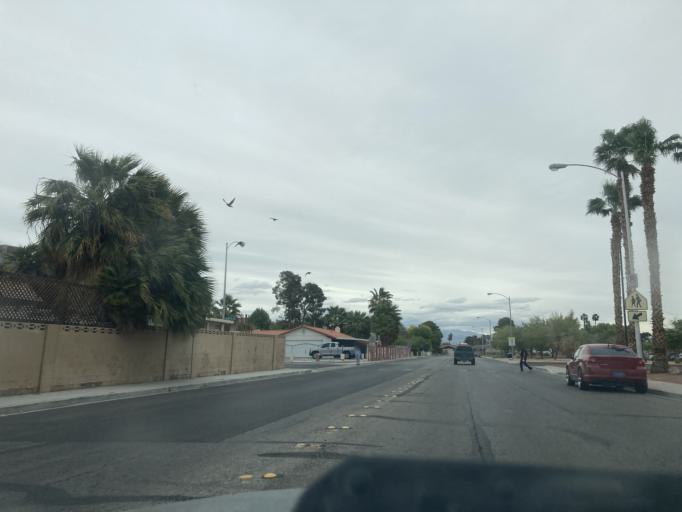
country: US
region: Nevada
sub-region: Clark County
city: Winchester
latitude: 36.1201
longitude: -115.0885
